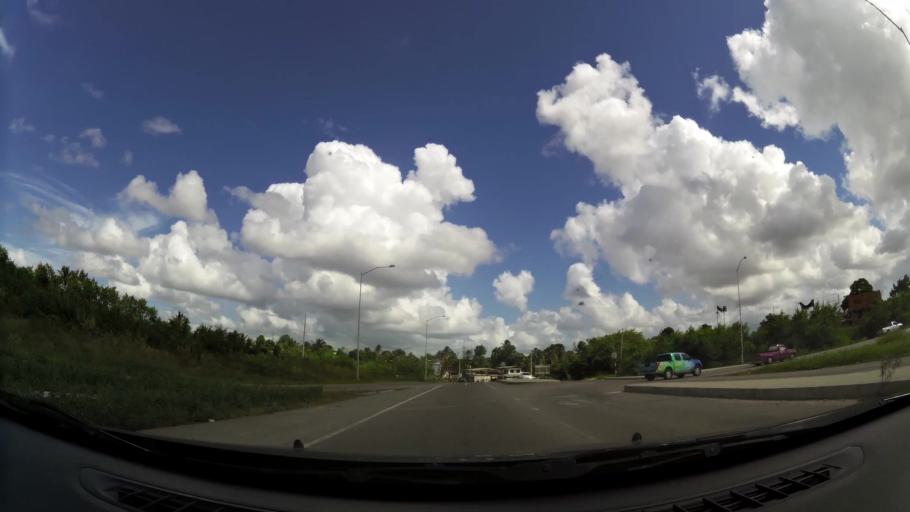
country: TT
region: City of San Fernando
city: Mon Repos
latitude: 10.2528
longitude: -61.4391
